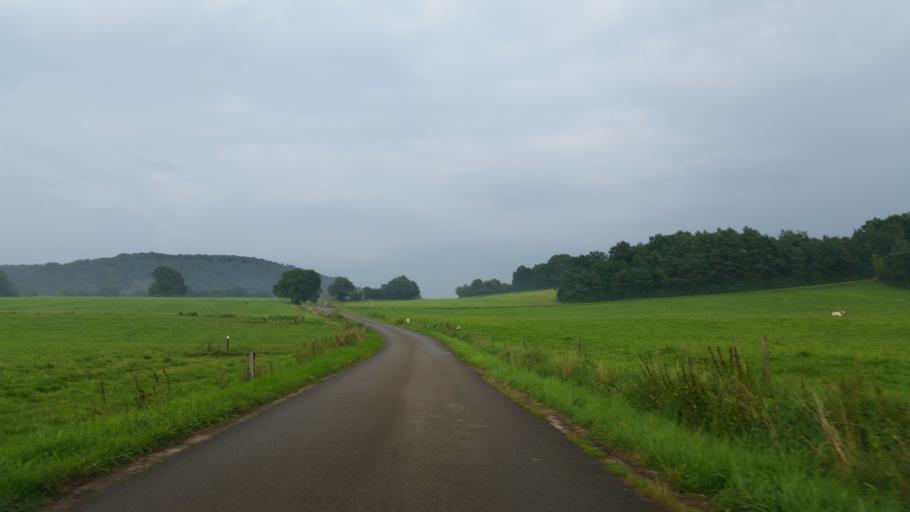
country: BE
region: Wallonia
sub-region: Province de Namur
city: Rochefort
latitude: 50.1267
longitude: 5.1986
